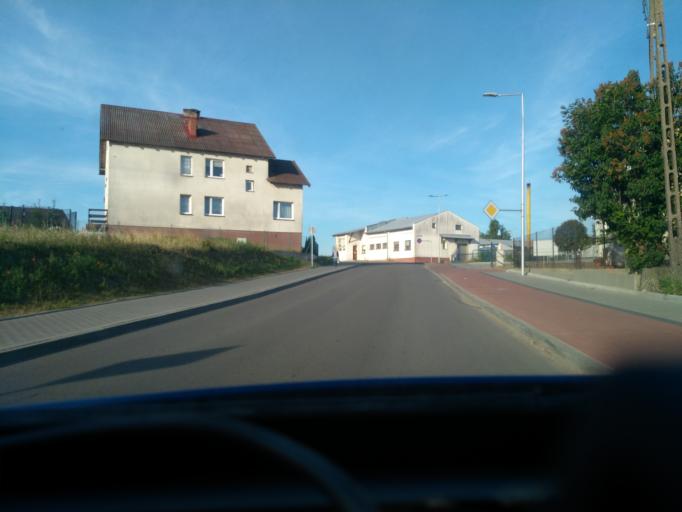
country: PL
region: Pomeranian Voivodeship
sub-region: Powiat kartuski
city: Banino
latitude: 54.3943
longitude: 18.4022
